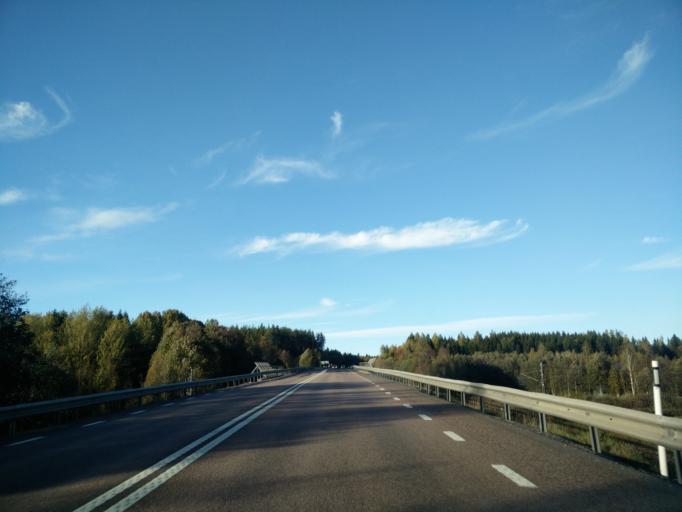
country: SE
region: Gaevleborg
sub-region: Nordanstigs Kommun
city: Bergsjoe
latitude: 62.0601
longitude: 17.2663
